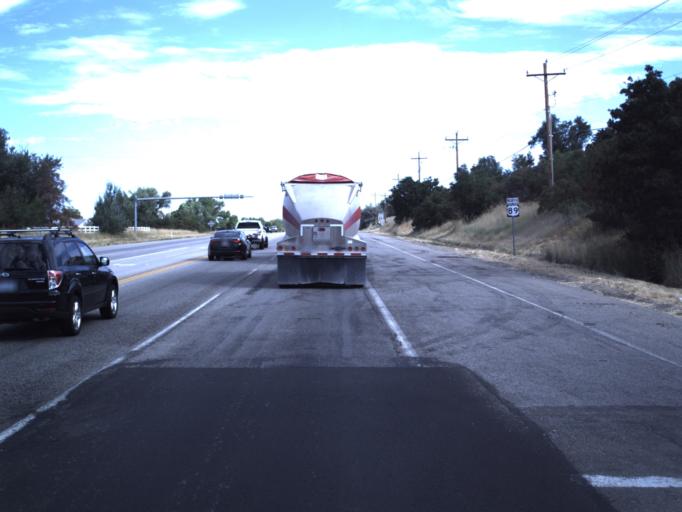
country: US
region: Utah
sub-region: Davis County
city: Fruit Heights
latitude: 41.0418
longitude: -111.9096
